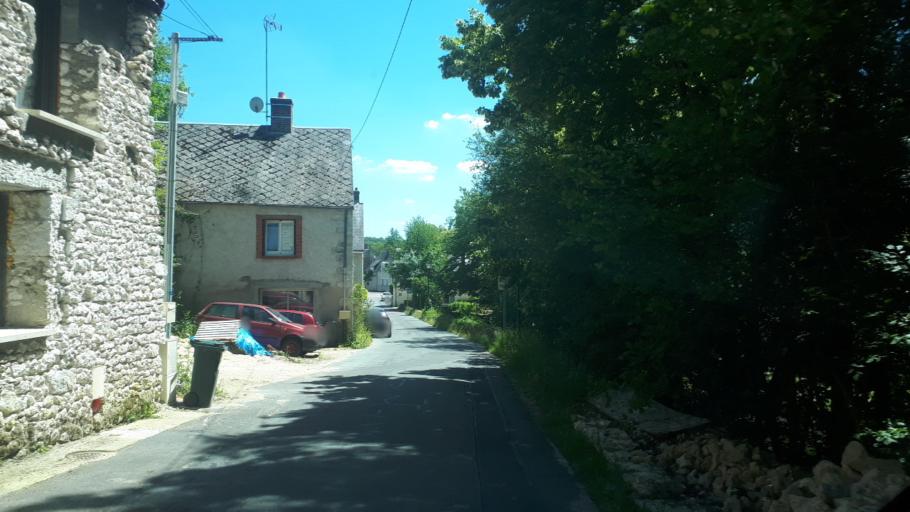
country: FR
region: Centre
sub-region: Departement du Loir-et-Cher
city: Saint-Sulpice-de-Pommeray
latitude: 47.5795
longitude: 1.2151
